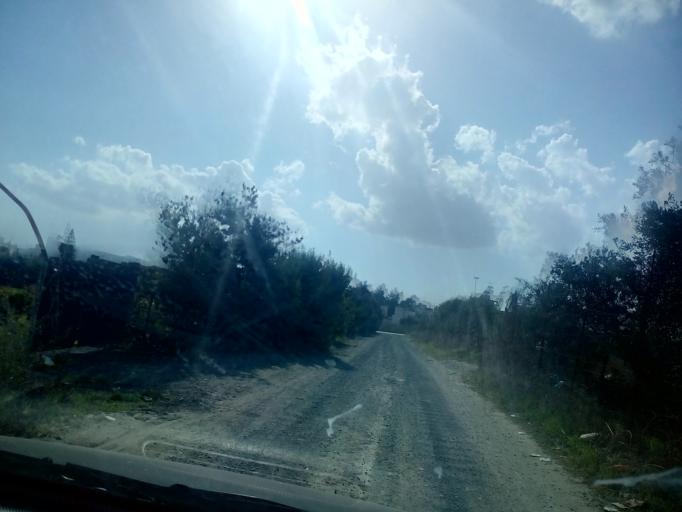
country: CY
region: Limassol
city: Ypsonas
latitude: 34.6629
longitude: 32.9675
